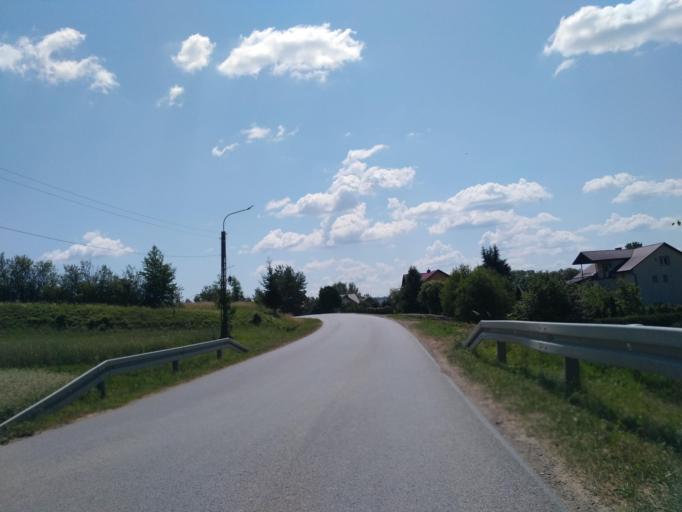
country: PL
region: Subcarpathian Voivodeship
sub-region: Powiat sanocki
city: Niebieszczany
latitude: 49.5135
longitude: 22.1421
